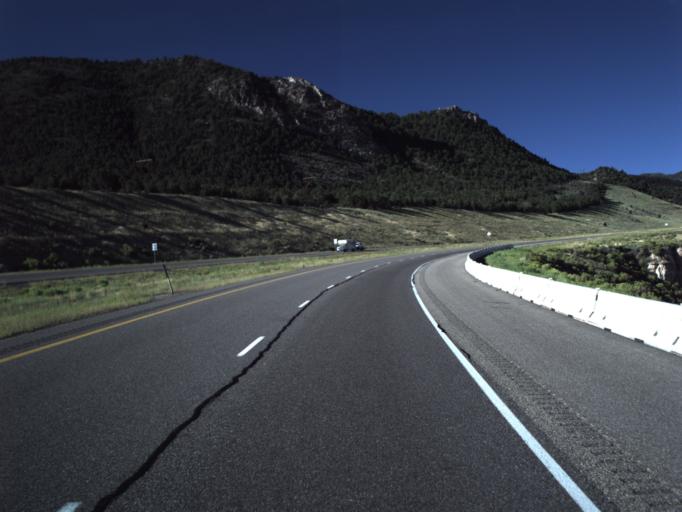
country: US
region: Utah
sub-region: Sevier County
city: Monroe
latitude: 38.5554
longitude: -112.3635
